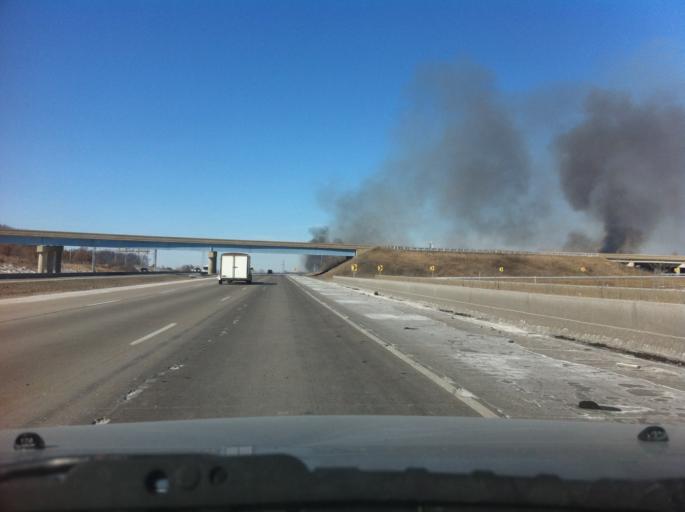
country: US
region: Wisconsin
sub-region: Columbia County
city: Portage
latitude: 43.4607
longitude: -89.4972
